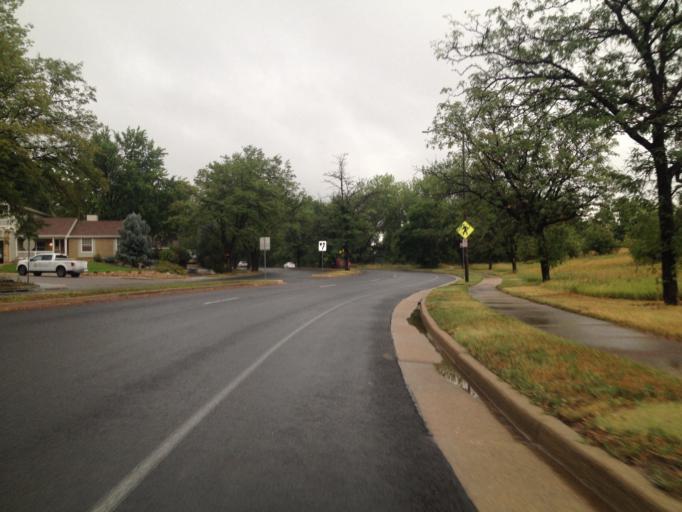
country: US
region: Colorado
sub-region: Boulder County
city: Louisville
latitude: 39.9842
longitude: -105.1442
